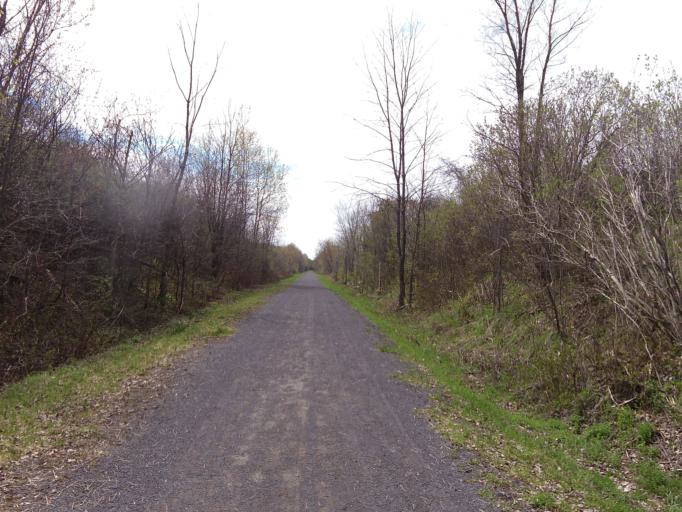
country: CA
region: Ontario
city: Hawkesbury
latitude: 45.5326
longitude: -74.6662
